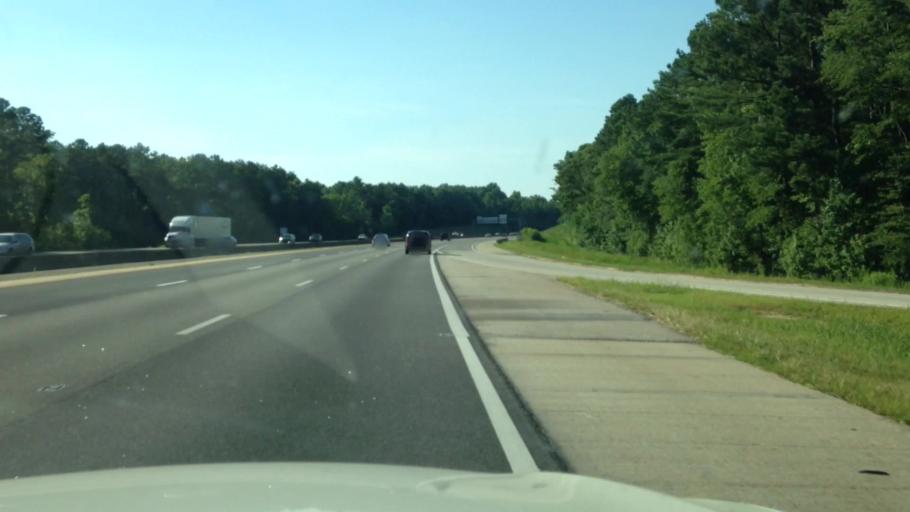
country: US
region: Virginia
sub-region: Chesterfield County
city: Enon
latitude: 37.3636
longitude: -77.3435
